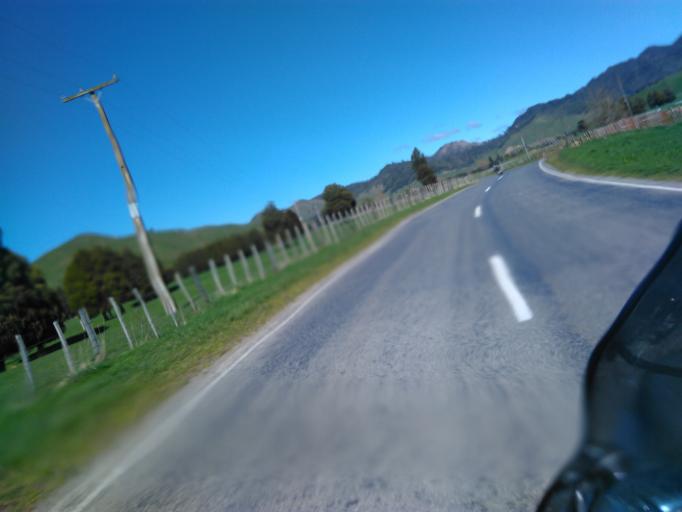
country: NZ
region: Bay of Plenty
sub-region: Opotiki District
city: Opotiki
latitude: -38.2890
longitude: 177.5323
